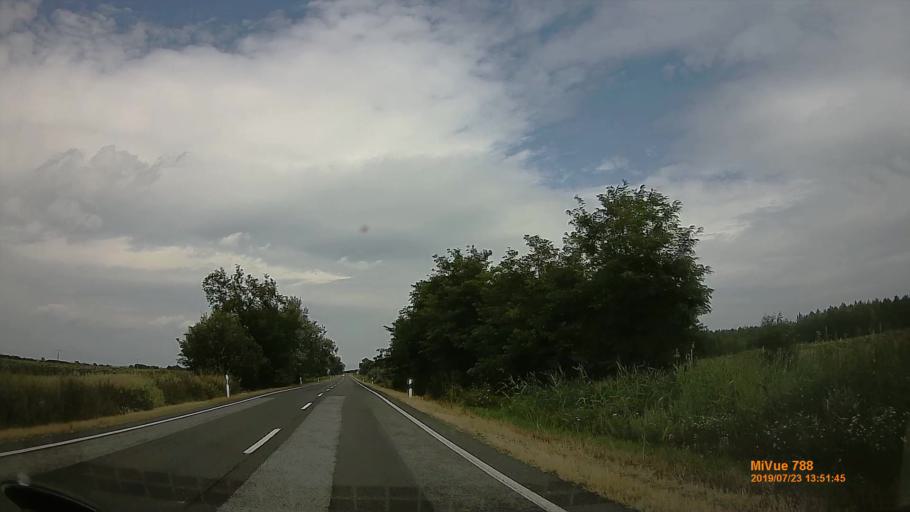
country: HU
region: Hajdu-Bihar
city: Polgar
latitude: 47.8928
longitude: 21.1536
